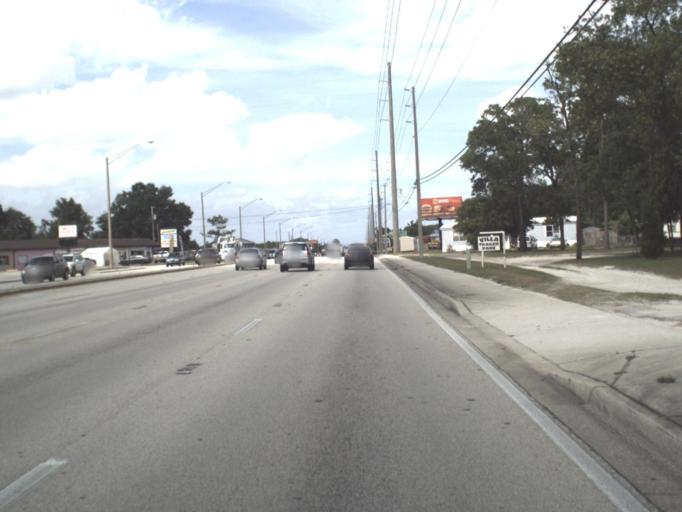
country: US
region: Florida
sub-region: Clay County
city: Lakeside
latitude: 30.1247
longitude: -81.7958
